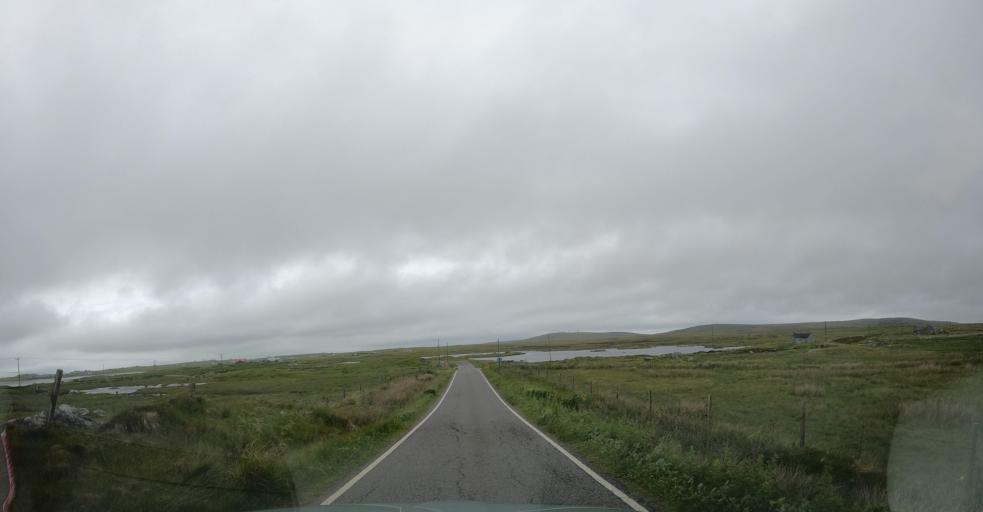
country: GB
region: Scotland
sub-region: Eilean Siar
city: Isle of North Uist
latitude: 57.5778
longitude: -7.4082
